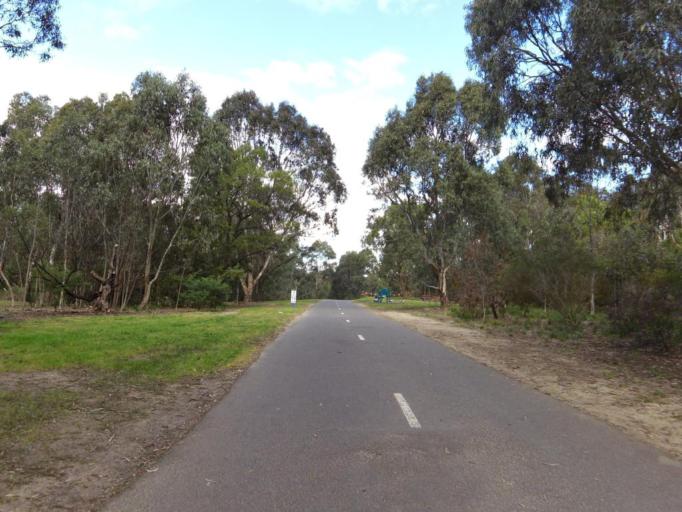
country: AU
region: Victoria
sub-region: Boroondara
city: Balwyn North
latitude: -37.7809
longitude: 145.0945
